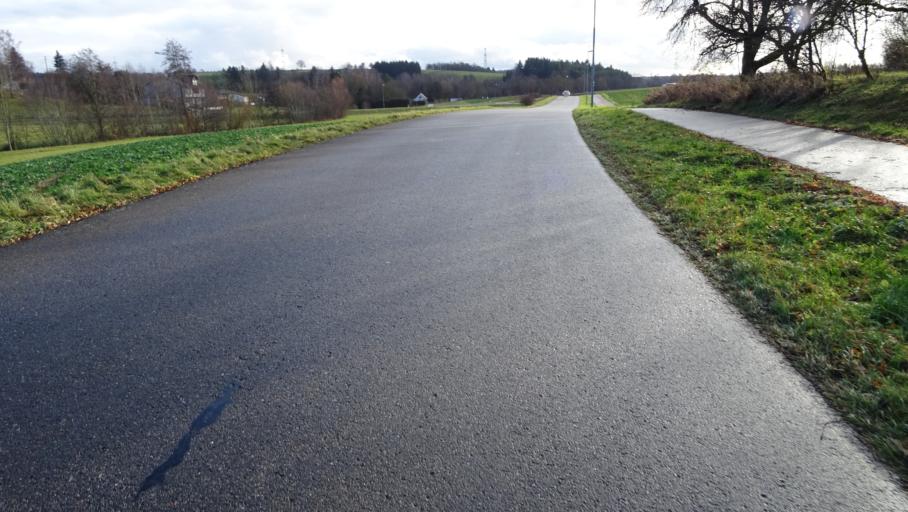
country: DE
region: Baden-Wuerttemberg
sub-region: Karlsruhe Region
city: Seckach
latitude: 49.4393
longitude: 9.2911
